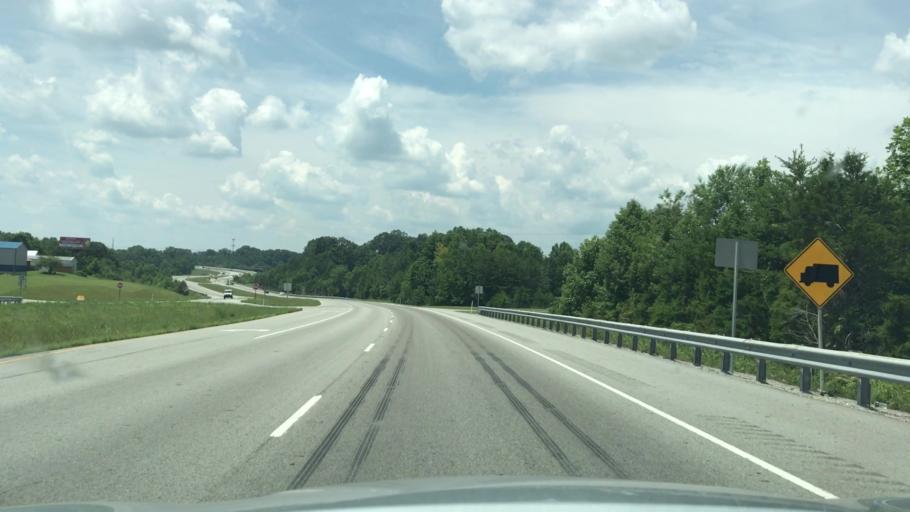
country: US
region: Tennessee
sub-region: Putnam County
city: Algood
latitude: 36.2072
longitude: -85.4481
